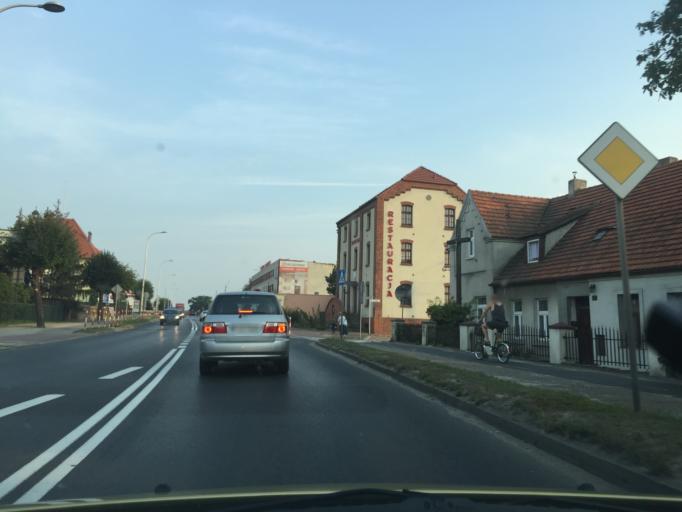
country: PL
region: Greater Poland Voivodeship
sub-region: Powiat jarocinski
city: Jarocin
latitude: 51.9672
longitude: 17.5061
